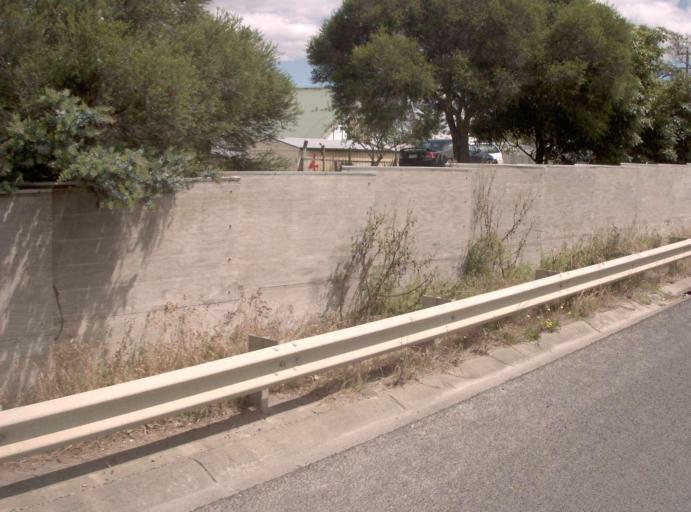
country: AU
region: Victoria
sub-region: Cardinia
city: Koo-Wee-Rup
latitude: -38.3968
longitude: 145.5382
